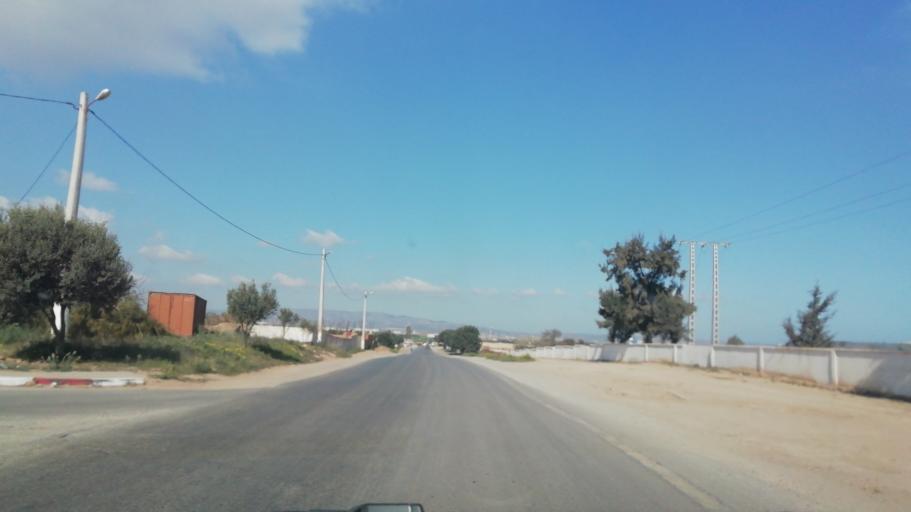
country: DZ
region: Oran
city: Ain el Bya
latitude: 35.7790
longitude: -0.2801
